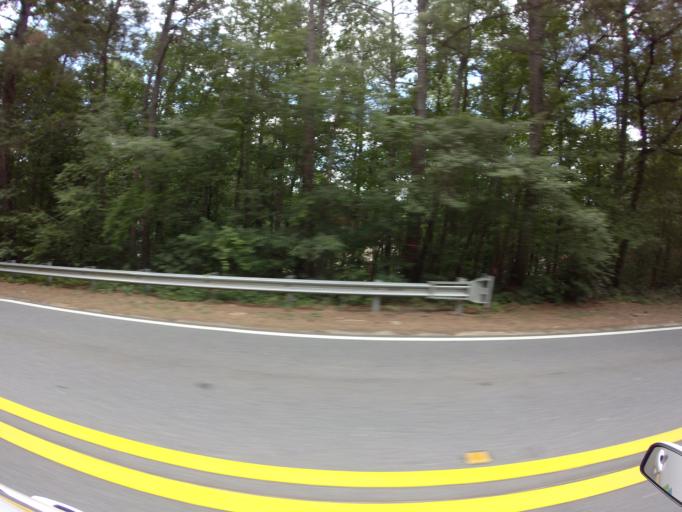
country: US
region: Georgia
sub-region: Fulton County
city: Johns Creek
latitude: 33.9945
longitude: -84.2587
